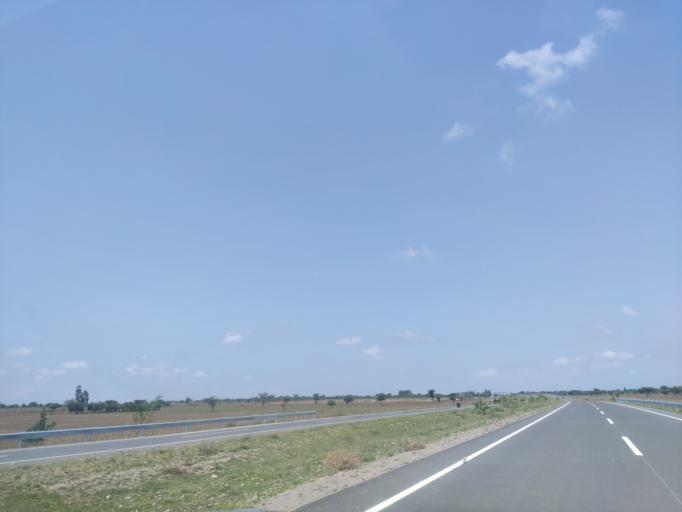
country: ET
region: Oromiya
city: Mojo
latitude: 8.2899
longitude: 38.9226
